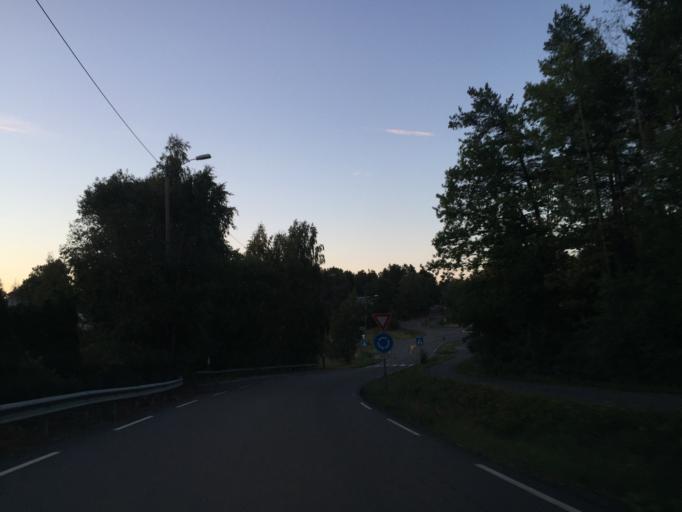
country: NO
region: Ostfold
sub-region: Moss
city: Moss
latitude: 59.5109
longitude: 10.6855
